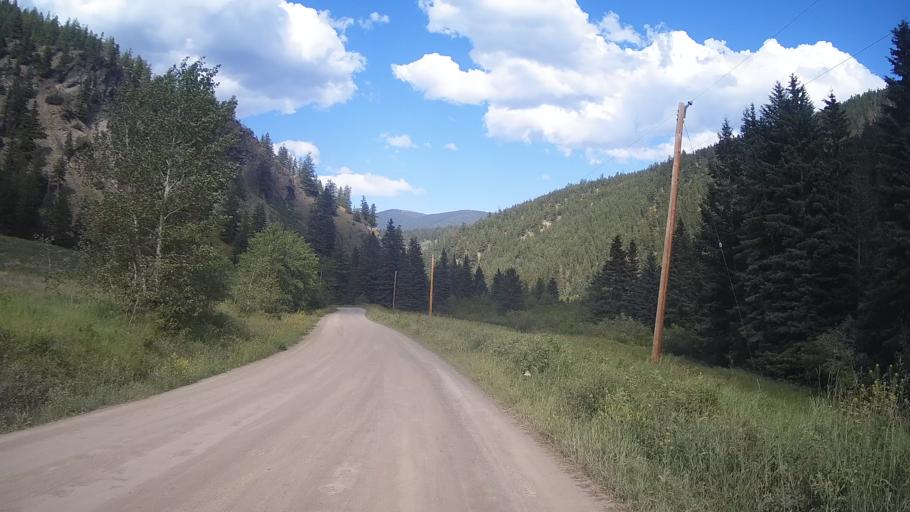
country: CA
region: British Columbia
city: Lillooet
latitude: 51.2542
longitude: -122.0081
